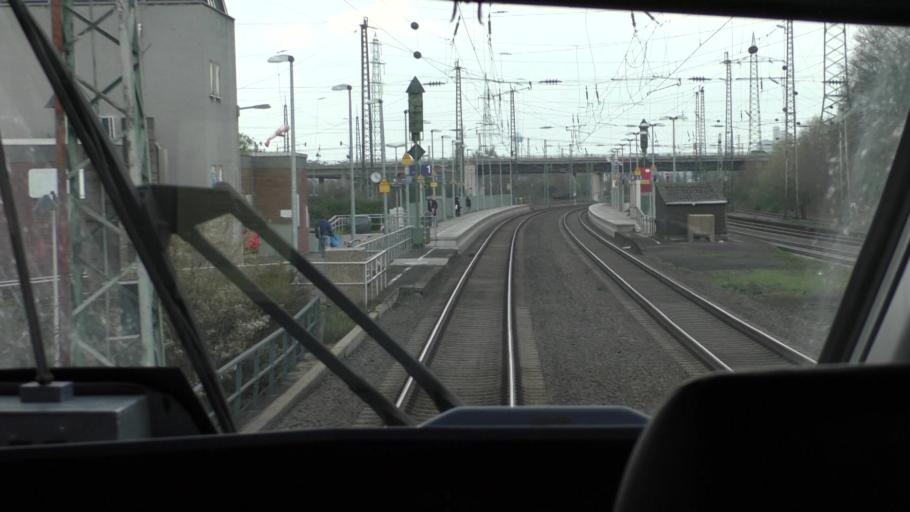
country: DE
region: North Rhine-Westphalia
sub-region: Regierungsbezirk Koln
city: Hurth
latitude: 50.8747
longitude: 6.9098
